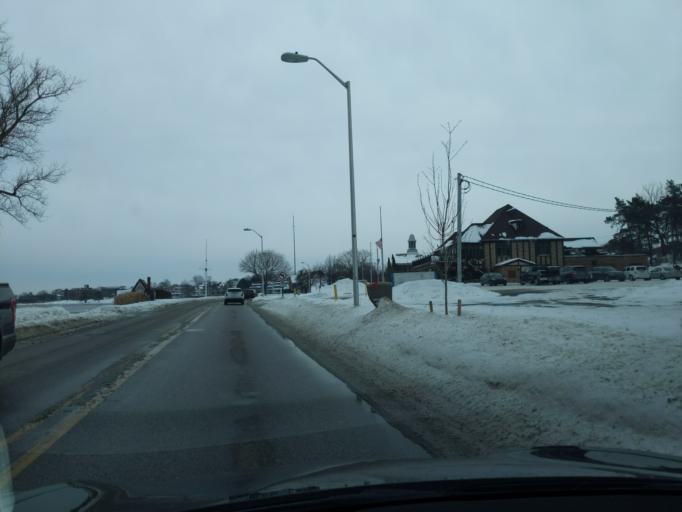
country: US
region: Michigan
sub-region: Ottawa County
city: Grand Haven
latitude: 43.0595
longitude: -86.2423
